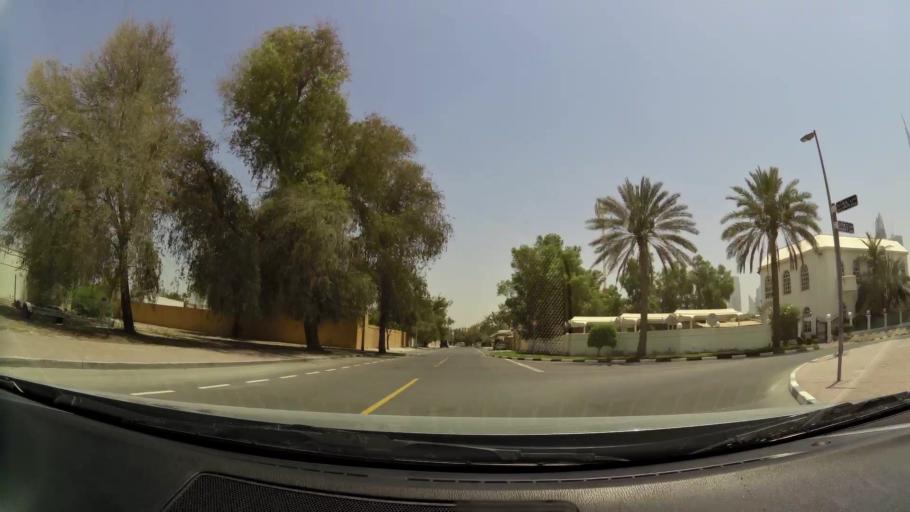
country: AE
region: Dubai
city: Dubai
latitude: 25.1989
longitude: 55.2557
